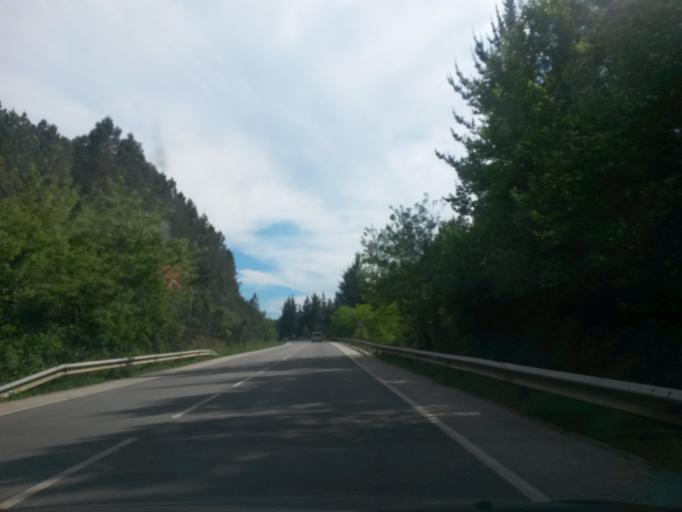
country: ES
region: Catalonia
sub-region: Provincia de Girona
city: Angles
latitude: 41.9406
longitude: 2.6421
